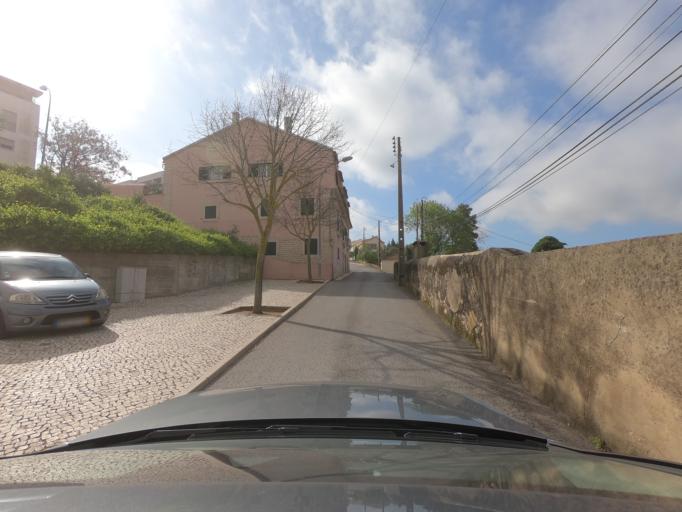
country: PT
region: Lisbon
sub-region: Oeiras
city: Barcarena
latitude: 38.7310
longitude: -9.2773
